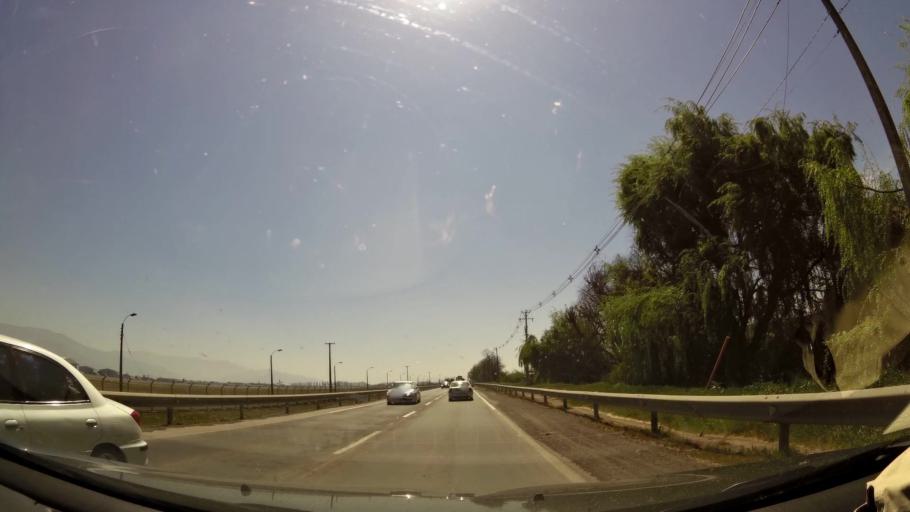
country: CL
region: Santiago Metropolitan
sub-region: Provincia de Santiago
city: Lo Prado
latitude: -33.3855
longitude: -70.7838
